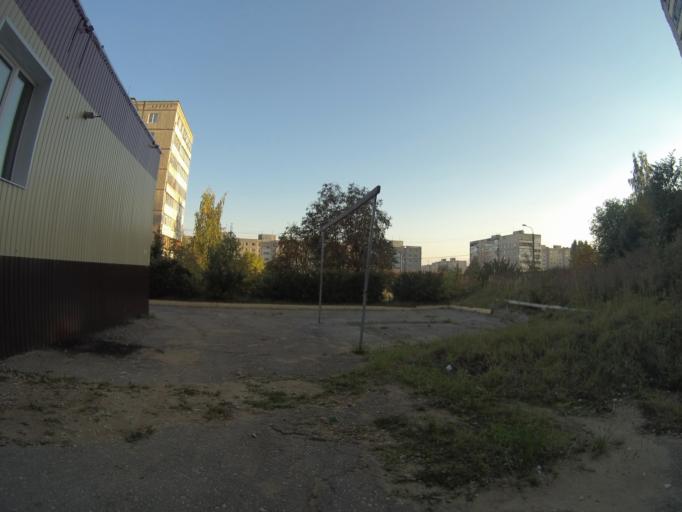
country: RU
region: Vladimir
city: Vladimir
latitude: 56.1088
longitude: 40.3536
